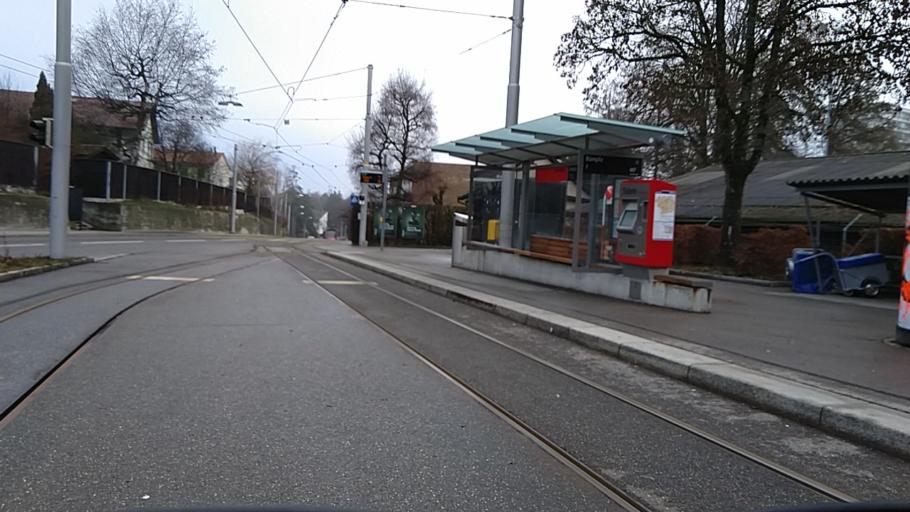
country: CH
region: Bern
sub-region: Bern-Mittelland District
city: Koniz
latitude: 46.9376
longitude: 7.3808
